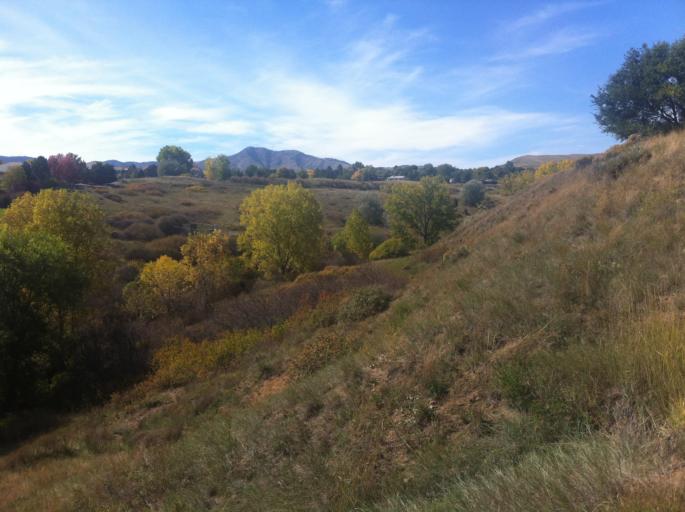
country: US
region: Colorado
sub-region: Jefferson County
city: Lakewood
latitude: 39.6754
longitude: -105.1283
